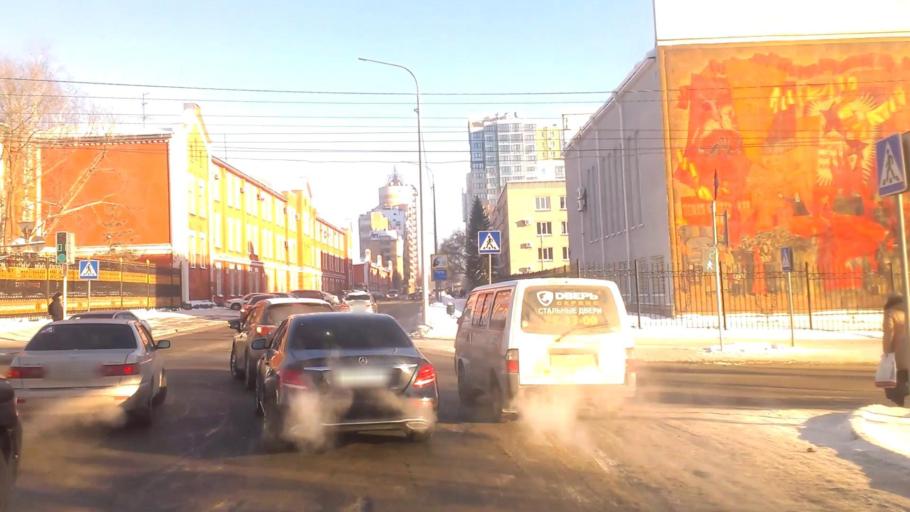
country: RU
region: Altai Krai
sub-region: Gorod Barnaulskiy
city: Barnaul
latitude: 53.3398
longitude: 83.7858
